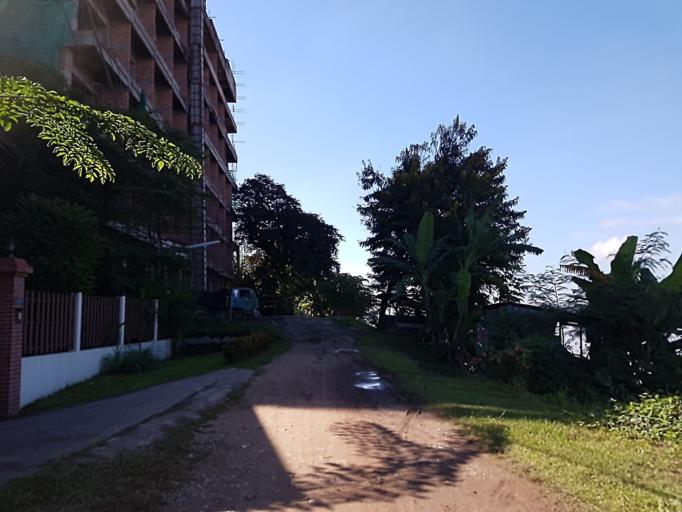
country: TH
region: Nong Khai
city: Si Chiang Mai
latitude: 17.9260
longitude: 102.6157
